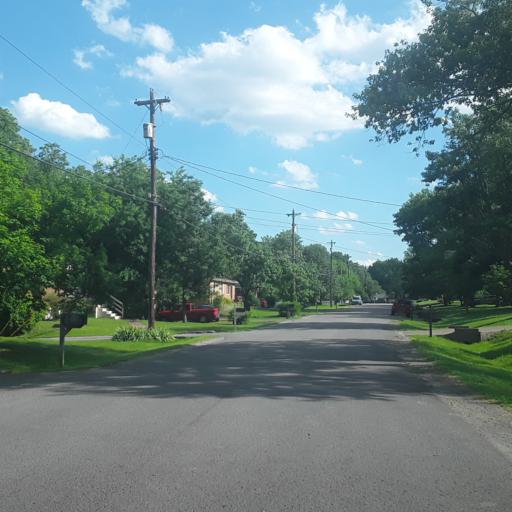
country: US
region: Tennessee
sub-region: Davidson County
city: Lakewood
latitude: 36.2060
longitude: -86.6345
